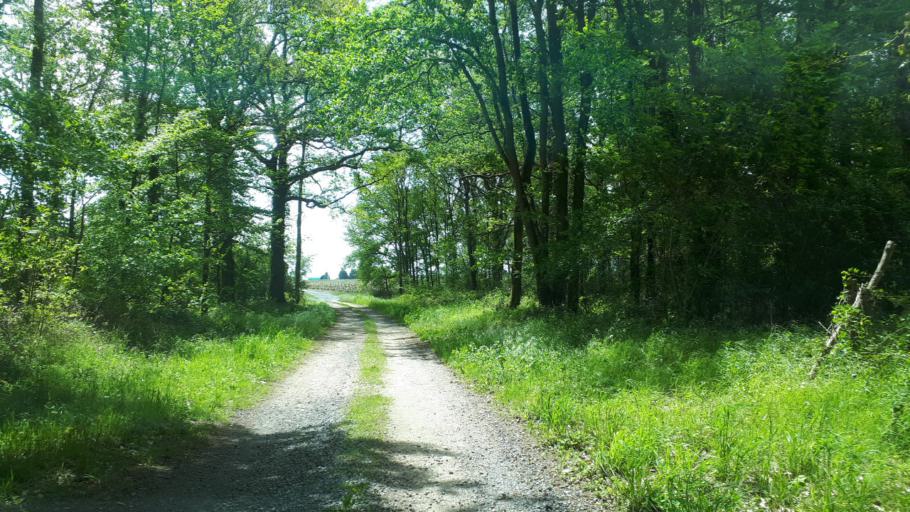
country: FR
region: Centre
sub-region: Departement du Loir-et-Cher
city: Saint-Romain-sur-Cher
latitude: 47.3598
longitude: 1.4295
